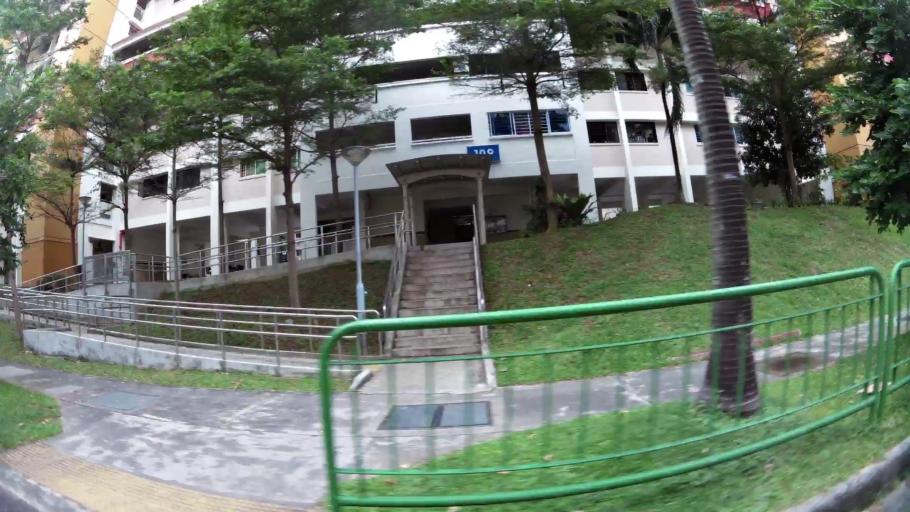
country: SG
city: Singapore
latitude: 1.3697
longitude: 103.8705
